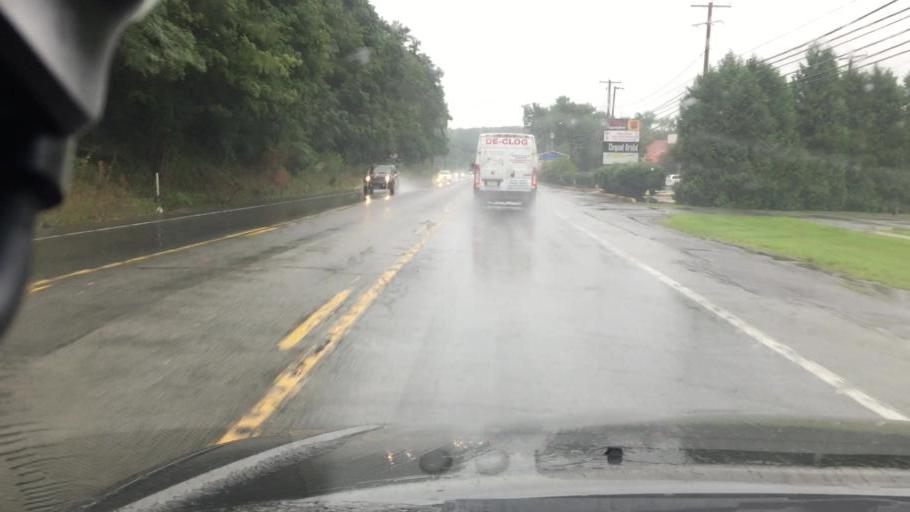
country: US
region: Pennsylvania
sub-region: Monroe County
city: Tannersville
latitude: 41.0198
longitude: -75.2967
